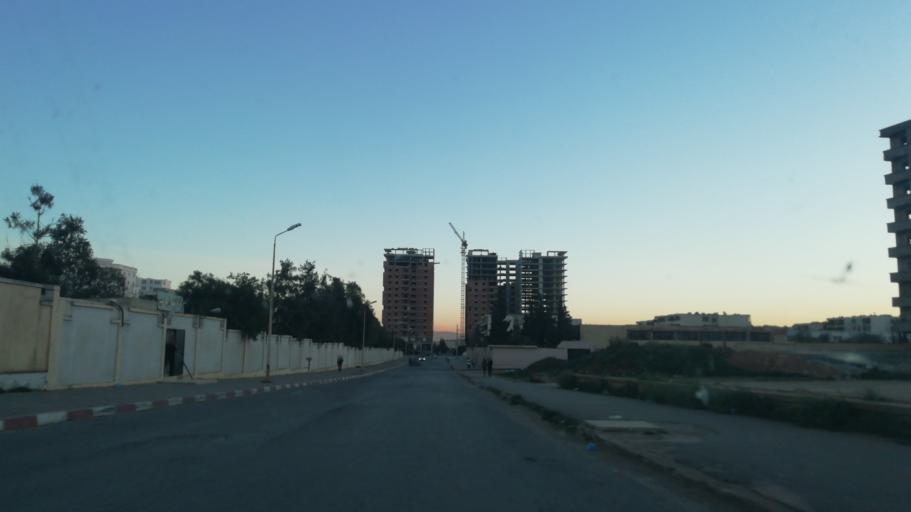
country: DZ
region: Oran
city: Bir el Djir
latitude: 35.7005
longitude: -0.5909
